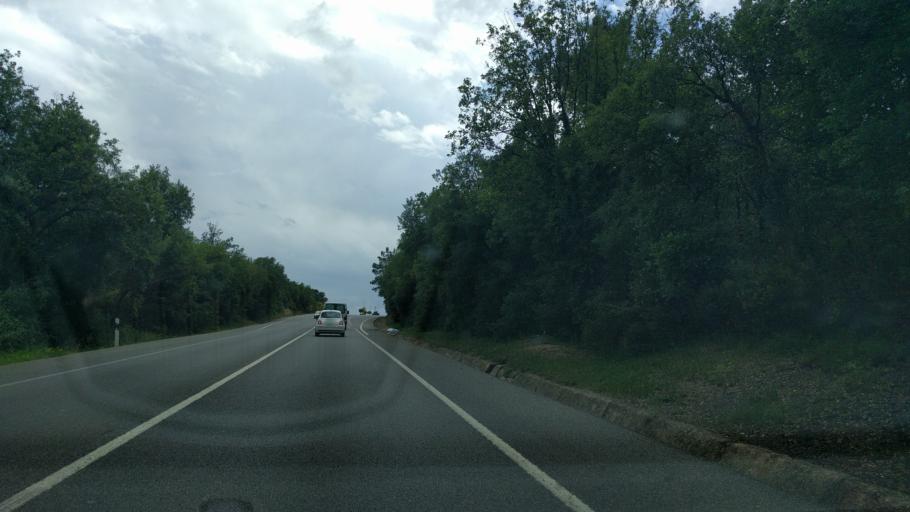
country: ES
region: Catalonia
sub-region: Provincia de Girona
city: Vidreres
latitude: 41.7602
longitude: 2.7583
